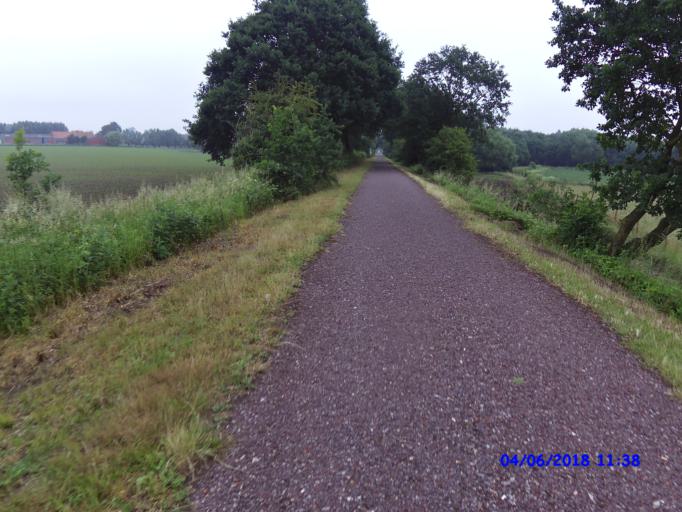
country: BE
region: Flanders
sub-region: Provincie West-Vlaanderen
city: Staden
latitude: 50.9683
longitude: 3.0017
